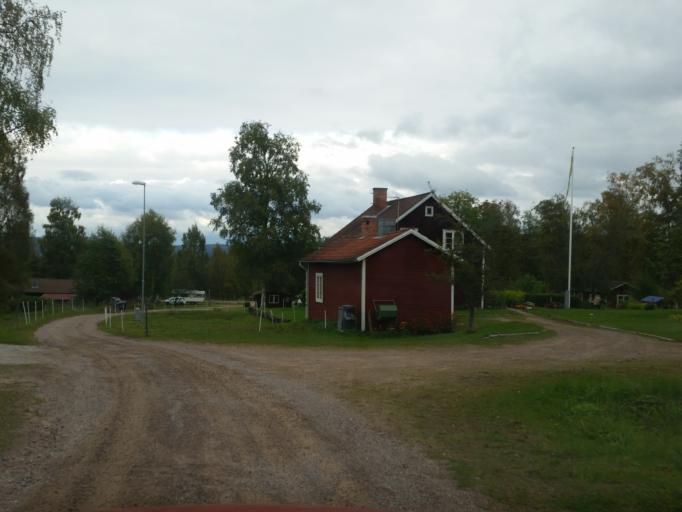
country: SE
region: Dalarna
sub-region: Leksand Municipality
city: Smedby
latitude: 60.6759
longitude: 15.1263
